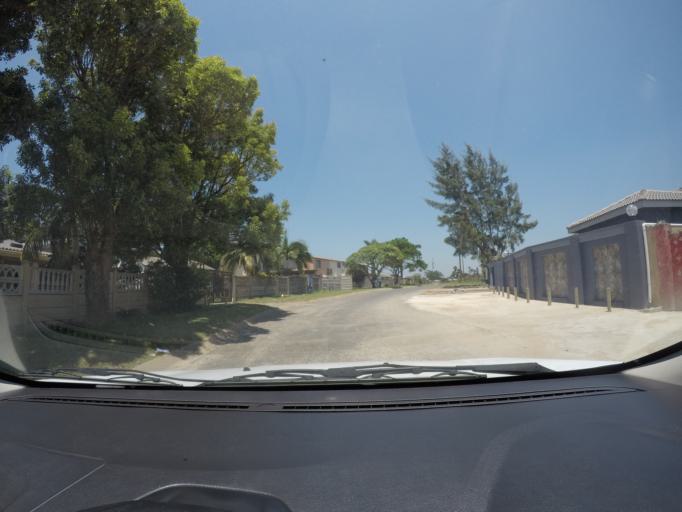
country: ZA
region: KwaZulu-Natal
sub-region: uThungulu District Municipality
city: eSikhawini
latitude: -28.8782
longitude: 31.9061
